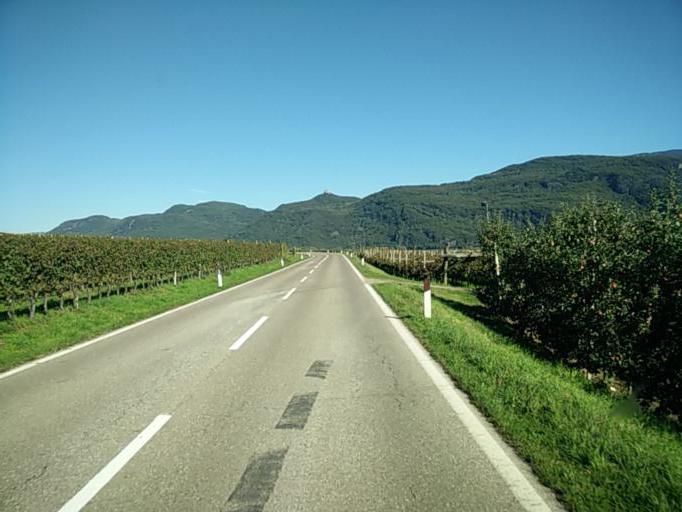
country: IT
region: Trentino-Alto Adige
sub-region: Bolzano
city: Termeno
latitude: 46.3574
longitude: 11.2510
